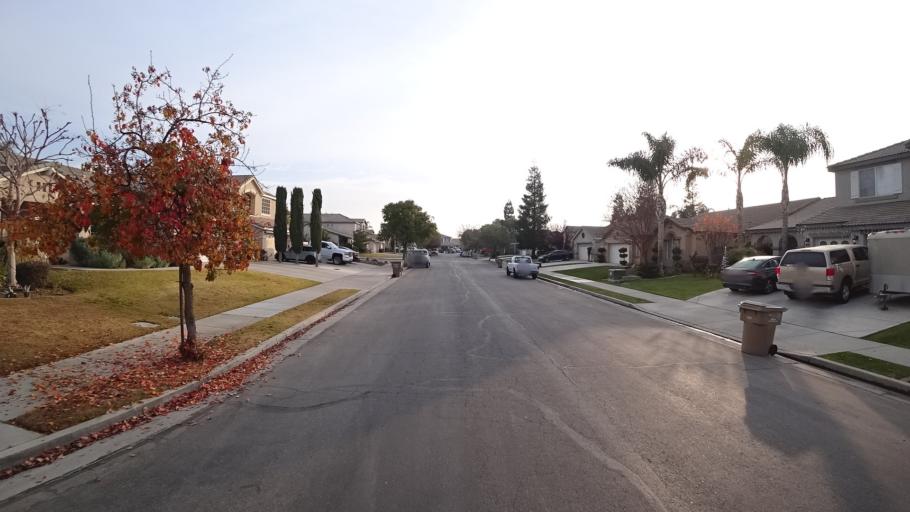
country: US
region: California
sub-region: Kern County
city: Greenacres
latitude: 35.4190
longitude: -119.1199
